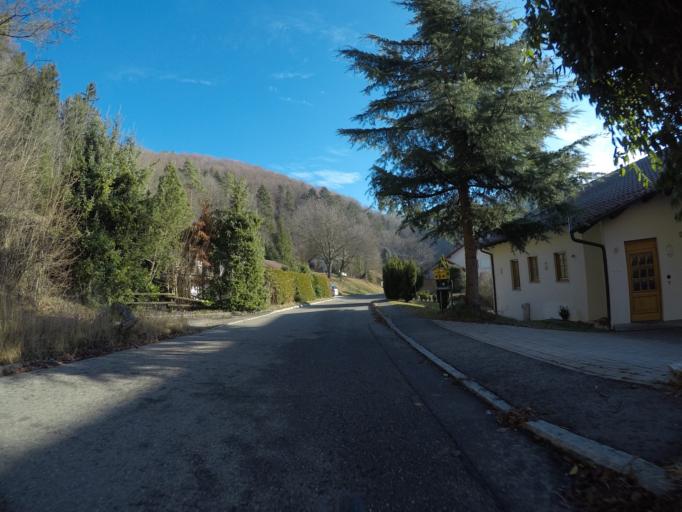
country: DE
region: Baden-Wuerttemberg
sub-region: Tuebingen Region
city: Pfullingen
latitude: 48.4485
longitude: 9.2602
